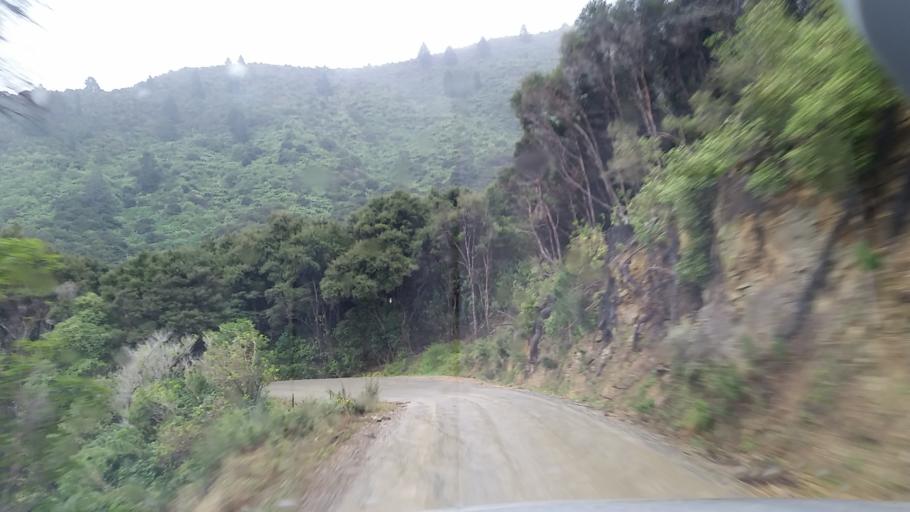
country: NZ
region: Marlborough
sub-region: Marlborough District
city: Picton
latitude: -41.1767
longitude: 174.0617
